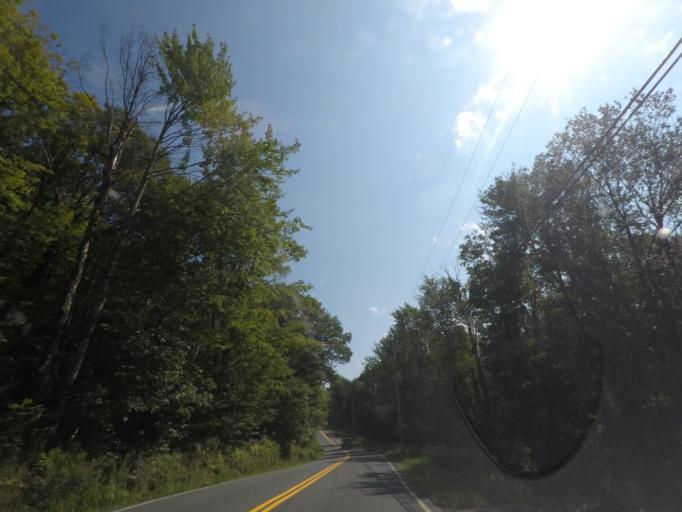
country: US
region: New York
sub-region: Rensselaer County
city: Poestenkill
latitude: 42.7249
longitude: -73.5100
